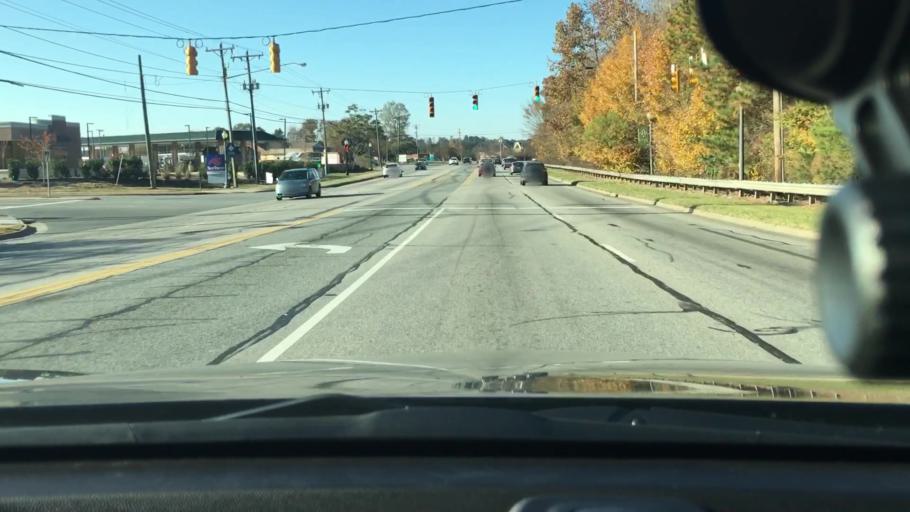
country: US
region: North Carolina
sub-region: Cabarrus County
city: Harrisburg
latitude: 35.3179
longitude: -80.6742
